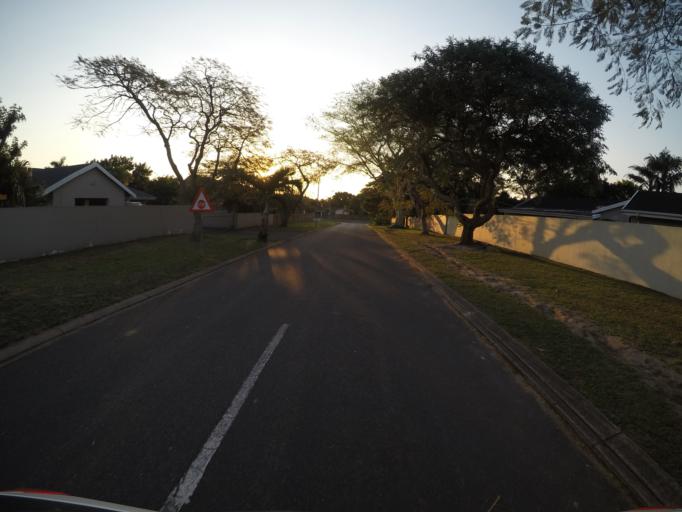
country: ZA
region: KwaZulu-Natal
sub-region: uThungulu District Municipality
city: Richards Bay
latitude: -28.7676
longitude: 32.1144
